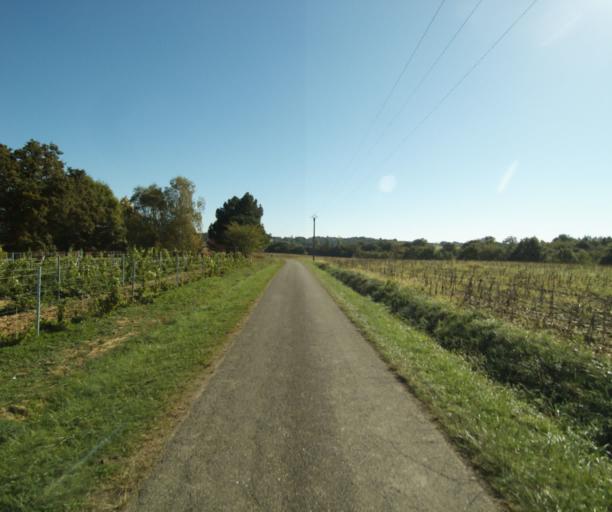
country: FR
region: Midi-Pyrenees
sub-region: Departement du Gers
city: Eauze
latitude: 43.8077
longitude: 0.1495
